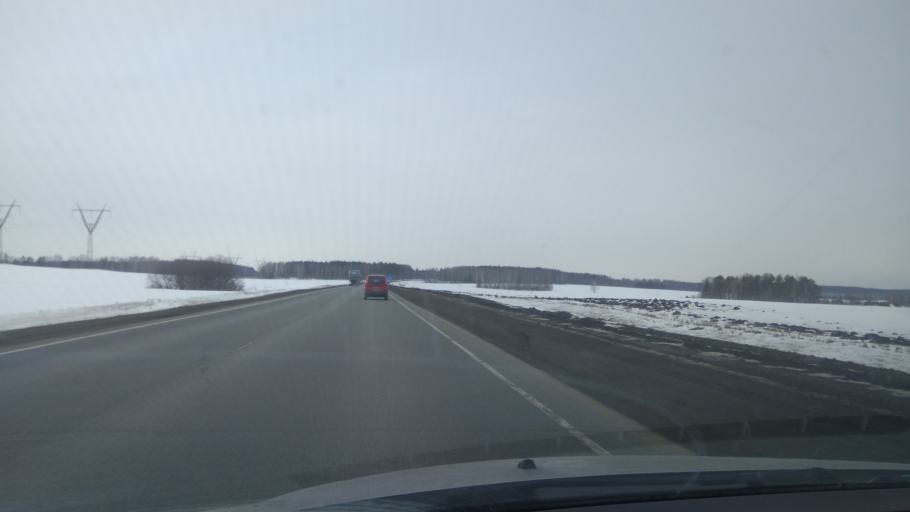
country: RU
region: Sverdlovsk
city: Ufimskiy
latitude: 56.7731
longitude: 58.0110
